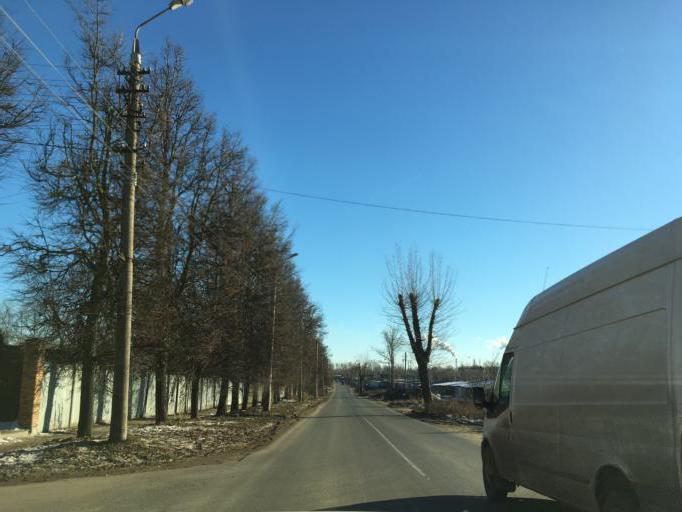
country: RU
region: Tula
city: Tula
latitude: 54.1823
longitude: 37.6963
